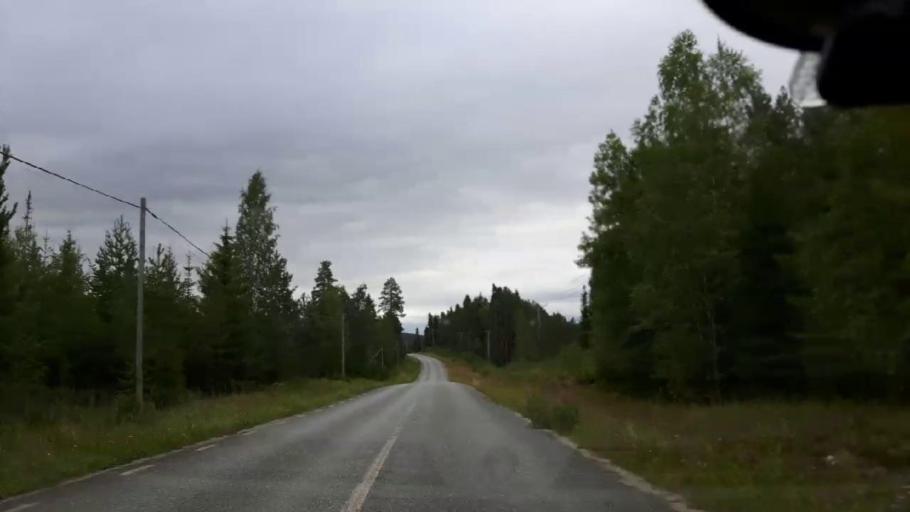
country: SE
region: Jaemtland
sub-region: Braecke Kommun
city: Braecke
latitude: 62.8808
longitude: 15.6180
